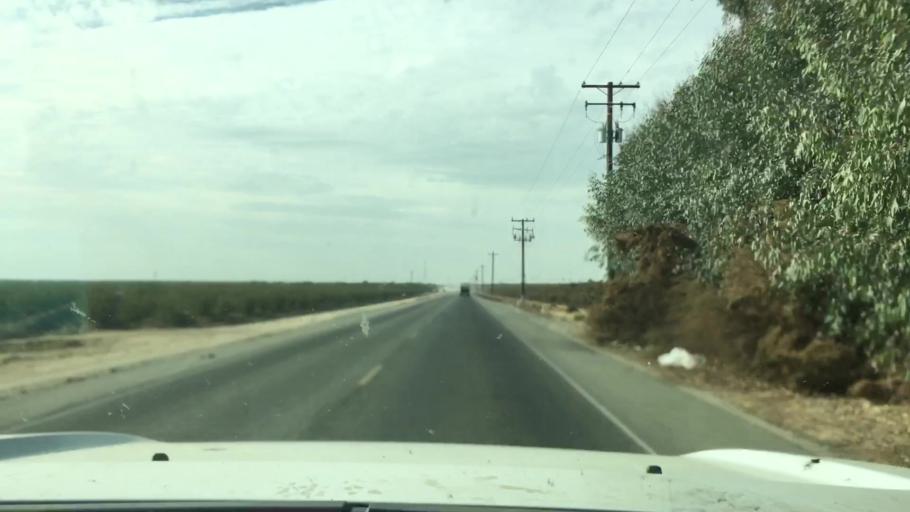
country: US
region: California
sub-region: Kern County
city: Buttonwillow
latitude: 35.5005
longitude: -119.4788
